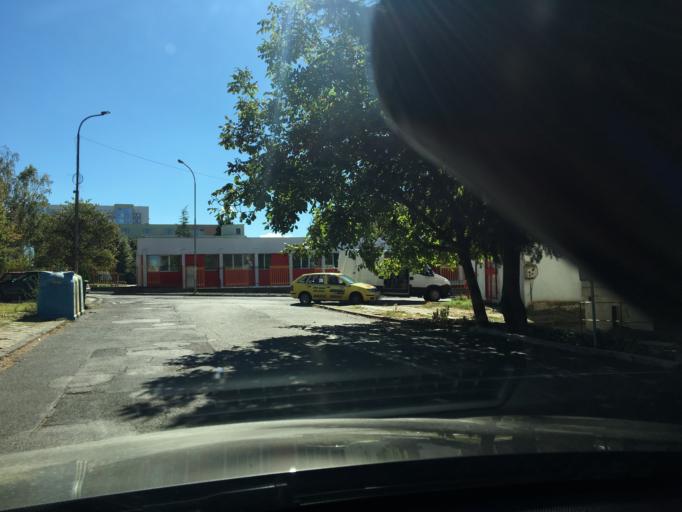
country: BG
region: Burgas
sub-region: Obshtina Burgas
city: Burgas
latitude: 42.5158
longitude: 27.4546
